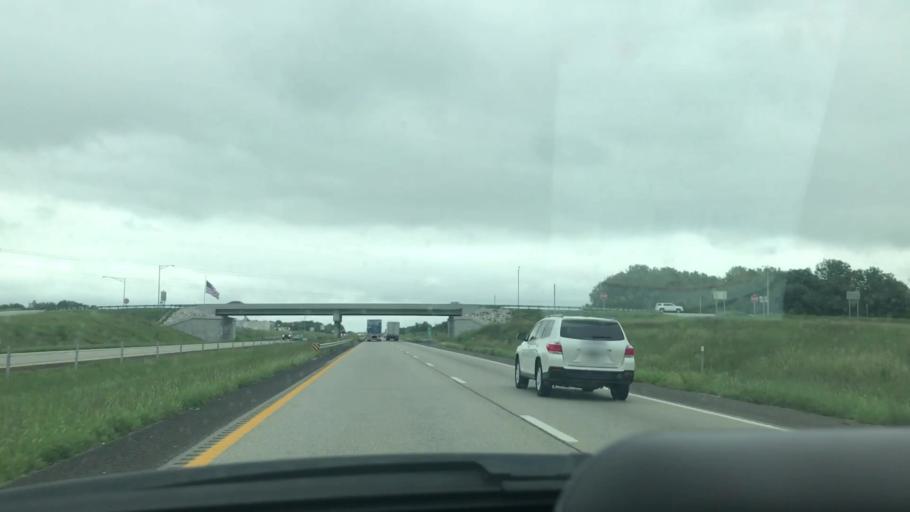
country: US
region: Missouri
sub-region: Greene County
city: Republic
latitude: 37.2001
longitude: -93.4249
